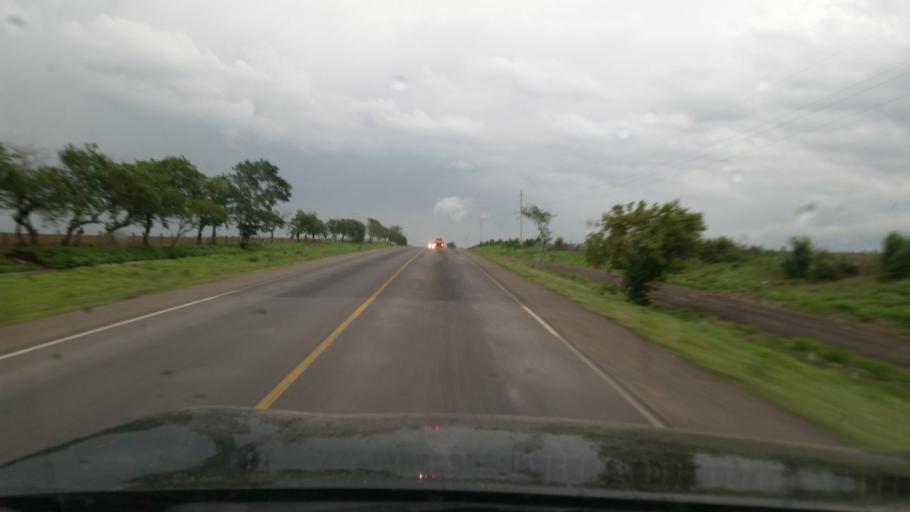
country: NI
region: Chinandega
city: Puerto Morazan
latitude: 12.7907
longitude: -87.0168
